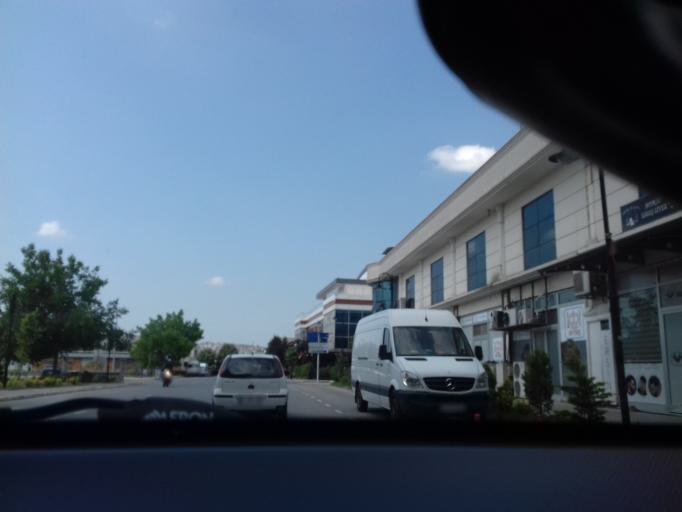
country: TR
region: Sakarya
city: Adapazari
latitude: 40.7140
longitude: 30.3610
